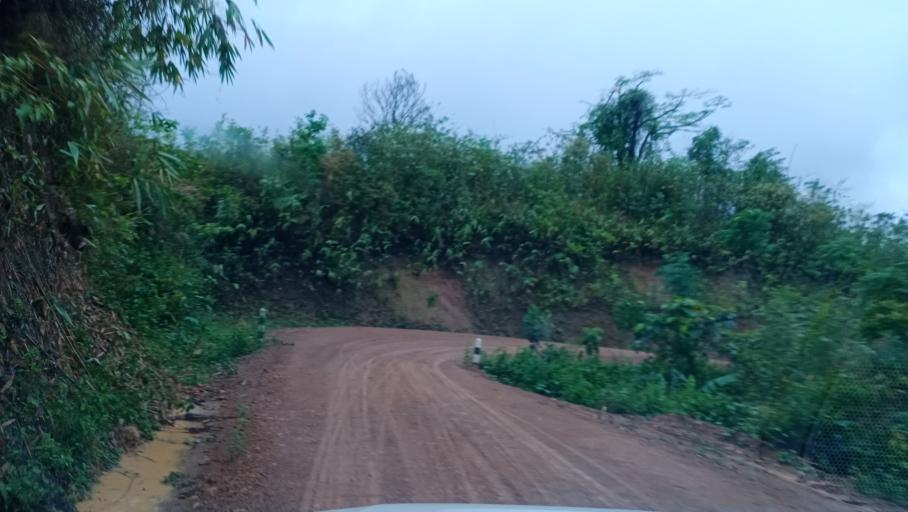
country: LA
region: Phongsali
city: Khoa
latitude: 21.3012
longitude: 102.7062
